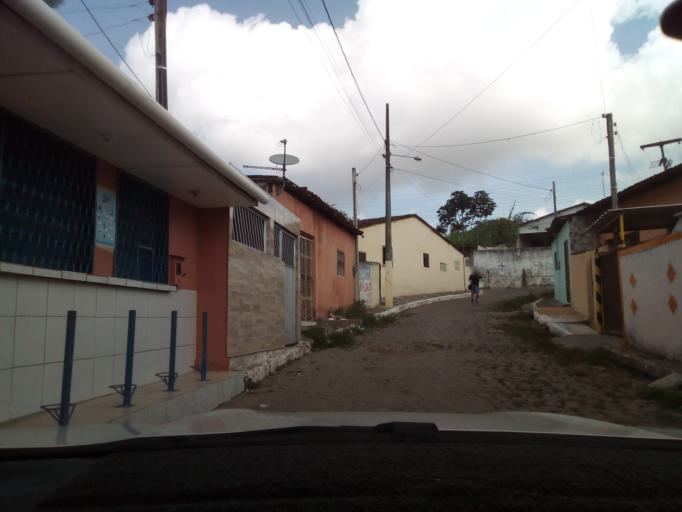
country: BR
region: Paraiba
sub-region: Bayeux
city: Bayeux
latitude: -7.1224
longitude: -34.9268
